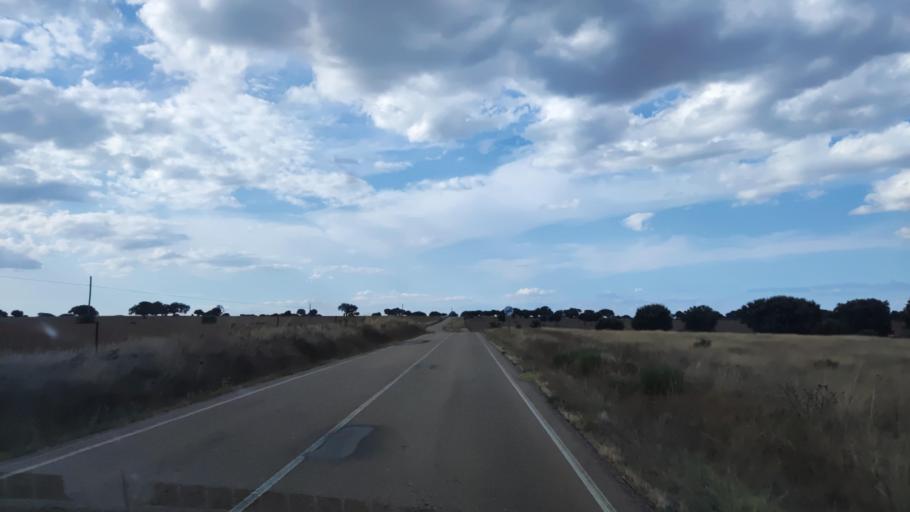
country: ES
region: Castille and Leon
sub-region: Provincia de Salamanca
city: Martiago
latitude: 40.4794
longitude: -6.4915
